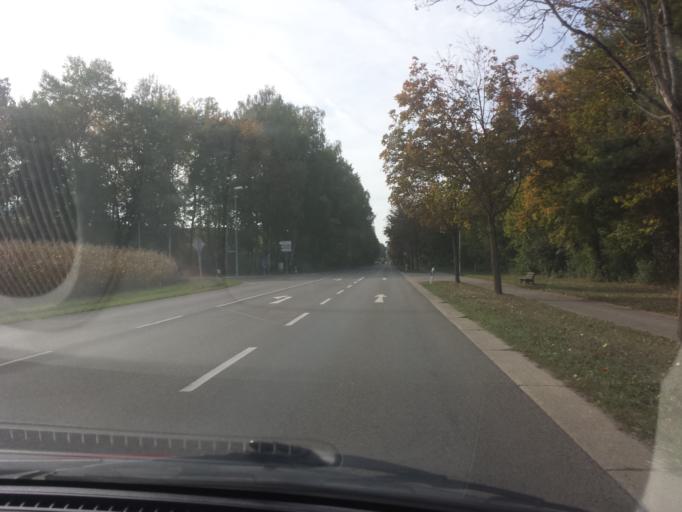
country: DE
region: Bavaria
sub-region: Upper Bavaria
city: Neuburg an der Donau
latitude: 48.7373
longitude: 11.2195
